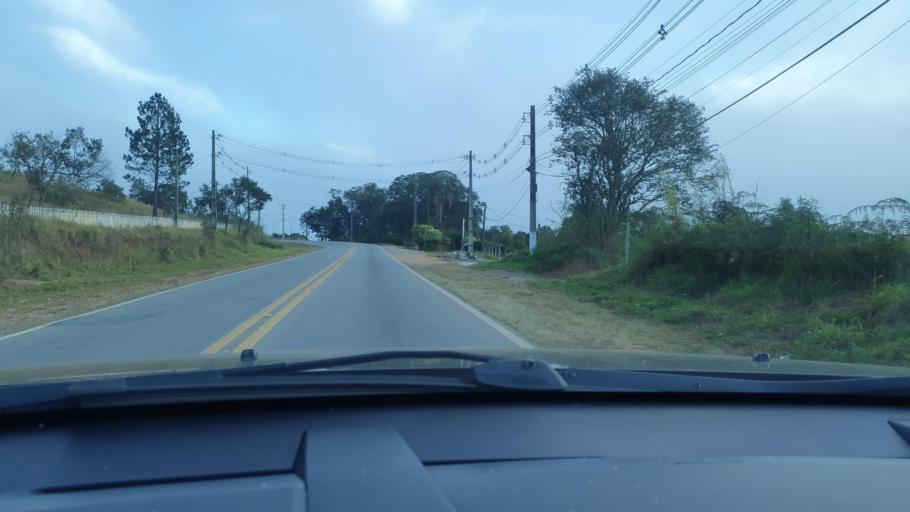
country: BR
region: Sao Paulo
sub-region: Ibiuna
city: Ibiuna
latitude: -23.6782
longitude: -47.2831
